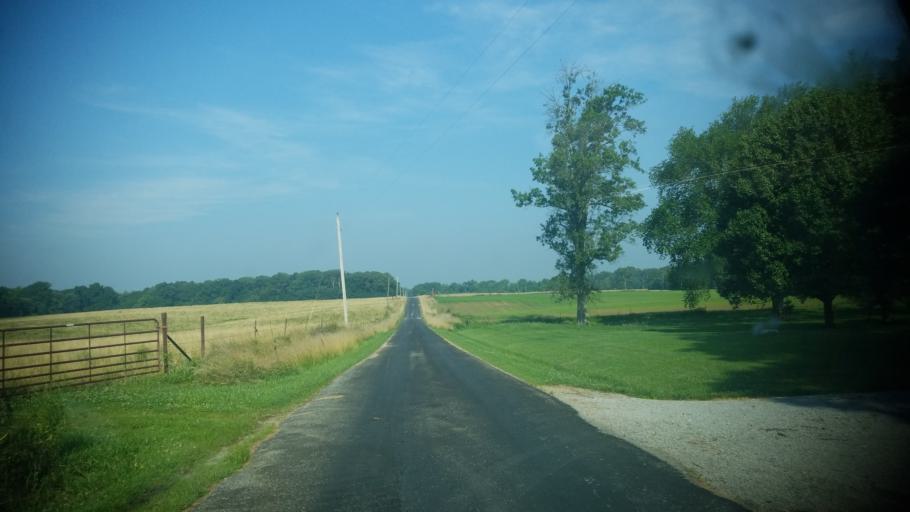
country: US
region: Illinois
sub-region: Clay County
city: Flora
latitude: 38.6026
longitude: -88.3919
